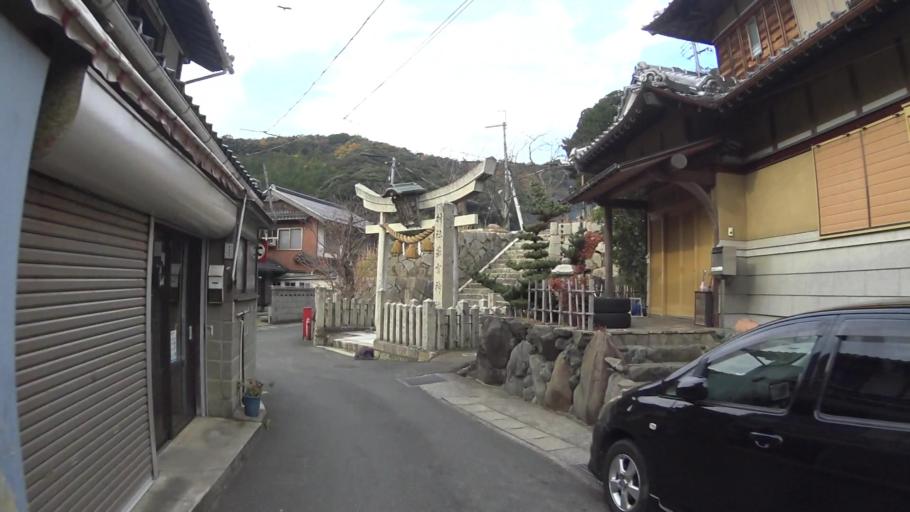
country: JP
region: Kyoto
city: Maizuru
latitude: 35.5702
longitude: 135.4286
